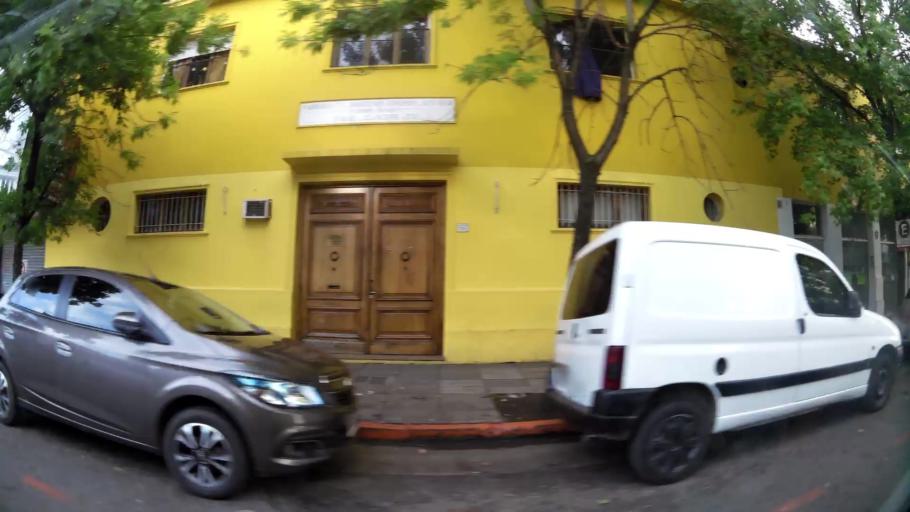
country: AR
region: Buenos Aires
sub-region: Partido de Moron
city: Moron
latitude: -34.6523
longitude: -58.6213
